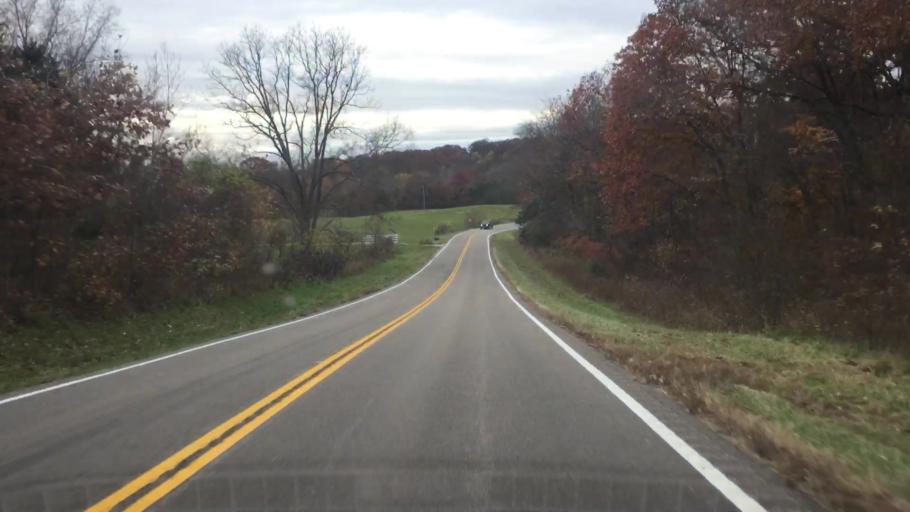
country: US
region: Missouri
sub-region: Gasconade County
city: Hermann
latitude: 38.7184
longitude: -91.6851
